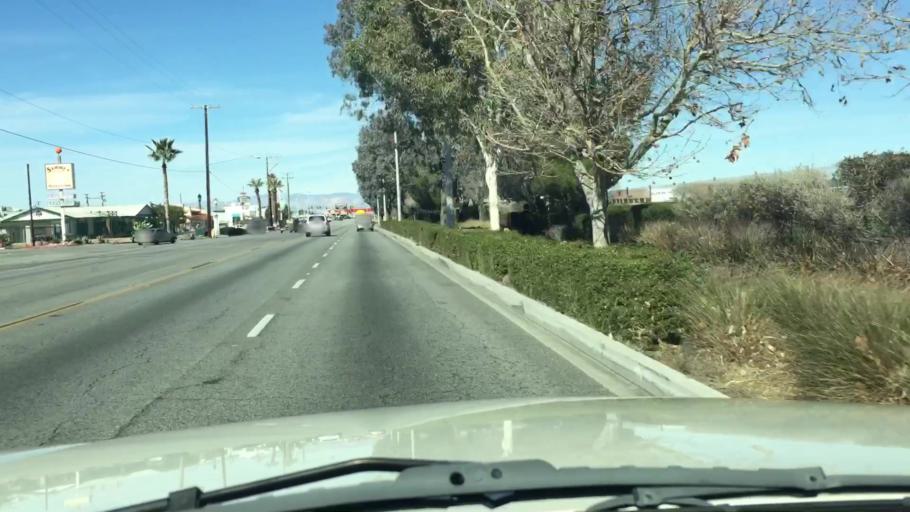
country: US
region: California
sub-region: Los Angeles County
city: Lancaster
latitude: 34.6851
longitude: -118.1344
